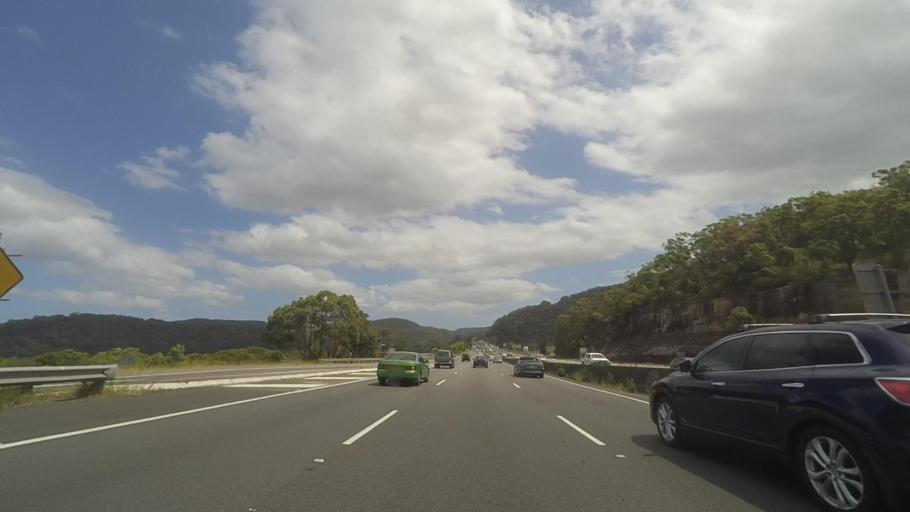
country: AU
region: New South Wales
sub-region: Hornsby Shire
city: Berowra
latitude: -33.5320
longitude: 151.2006
